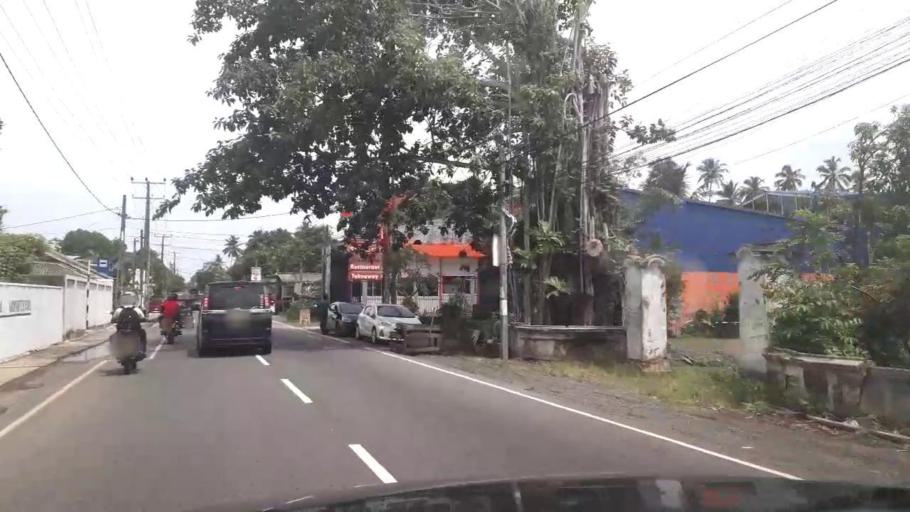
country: LK
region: Western
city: Panadura
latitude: 6.7342
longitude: 79.9044
